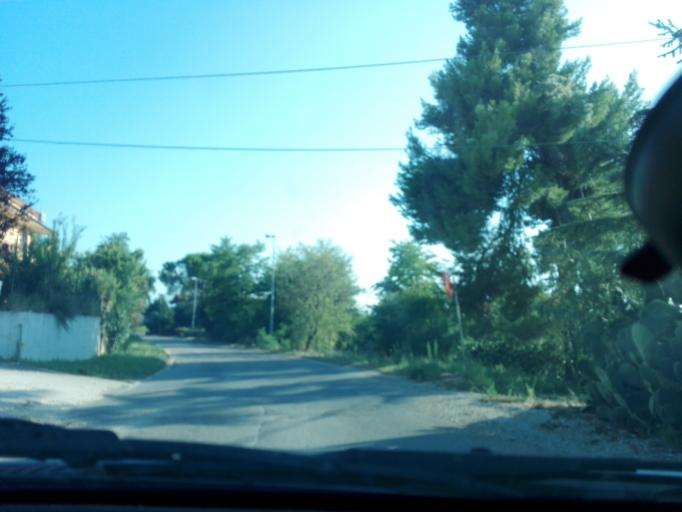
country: IT
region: Abruzzo
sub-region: Provincia di Pescara
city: Cappelle sul Tavo
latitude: 42.4591
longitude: 14.0992
